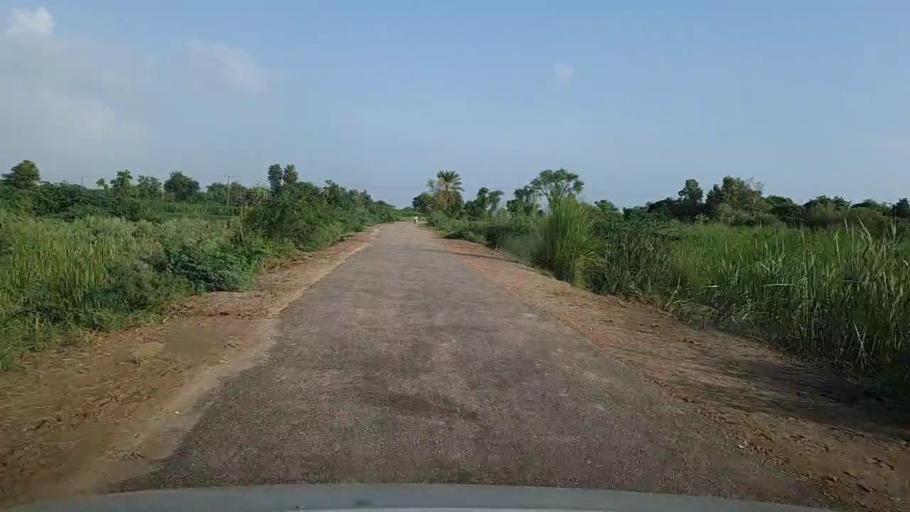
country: PK
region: Sindh
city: Pad Idan
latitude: 26.8022
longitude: 68.2356
